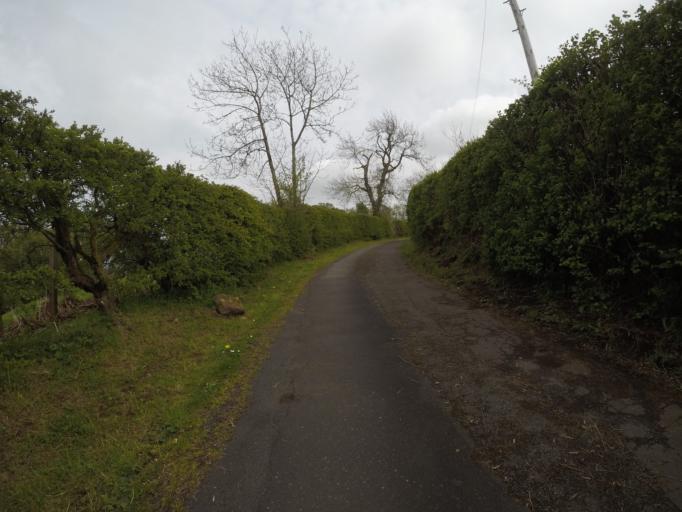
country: GB
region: Scotland
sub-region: East Renfrewshire
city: Newton Mearns
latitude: 55.7573
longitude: -4.3366
